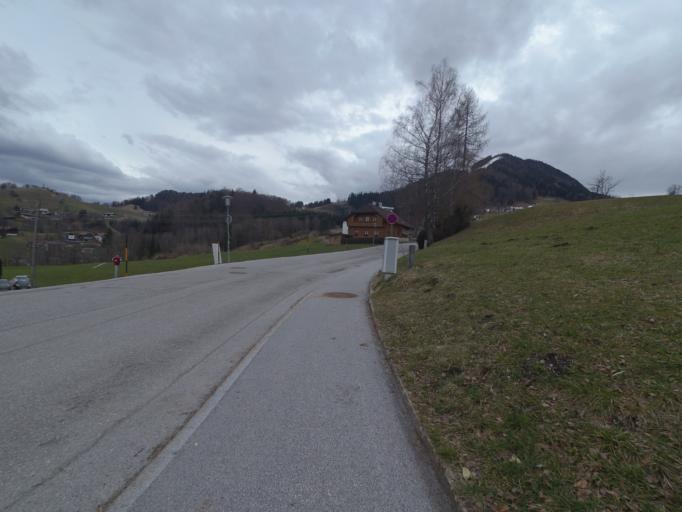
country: AT
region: Salzburg
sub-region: Politischer Bezirk Hallein
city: Hallein
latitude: 47.6637
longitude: 13.0904
